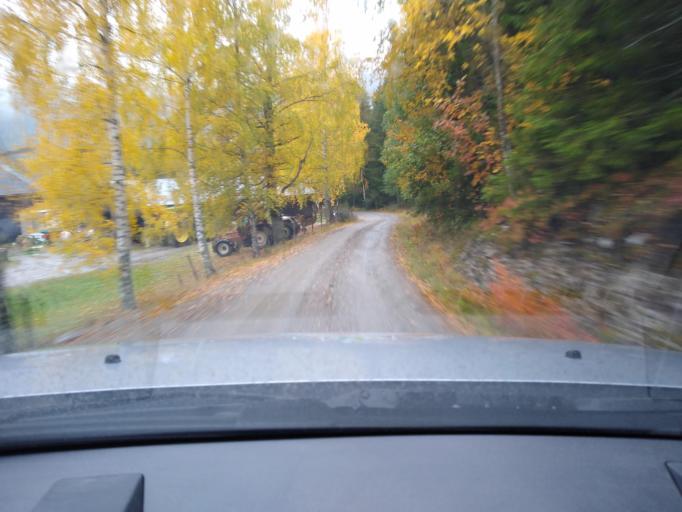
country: NO
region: Oppland
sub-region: Ringebu
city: Ringebu
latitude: 61.5507
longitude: 10.1565
